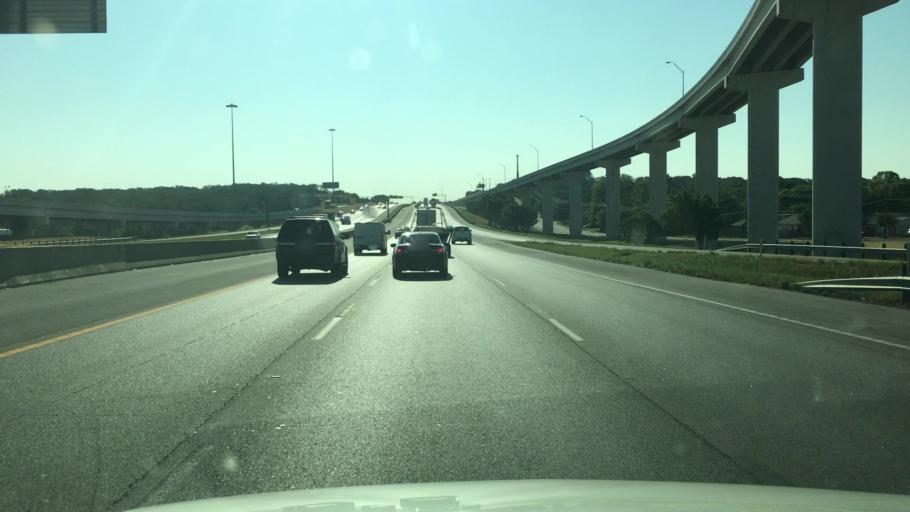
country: US
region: Texas
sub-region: Tarrant County
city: Richland Hills
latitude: 32.7597
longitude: -97.2108
